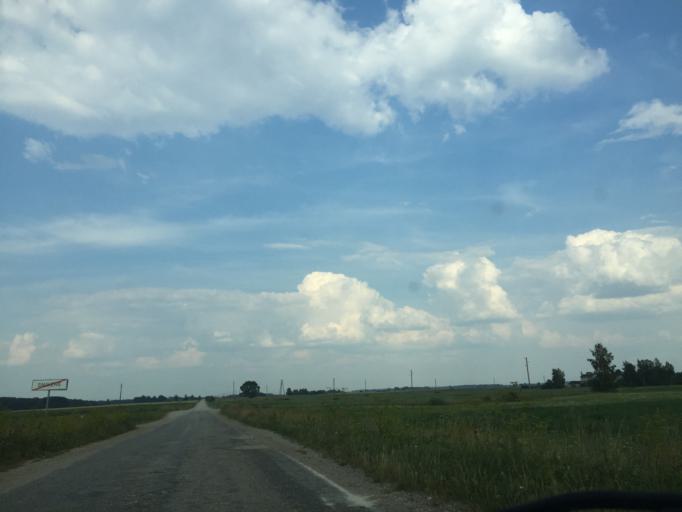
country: LT
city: Zagare
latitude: 56.4011
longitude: 23.1214
